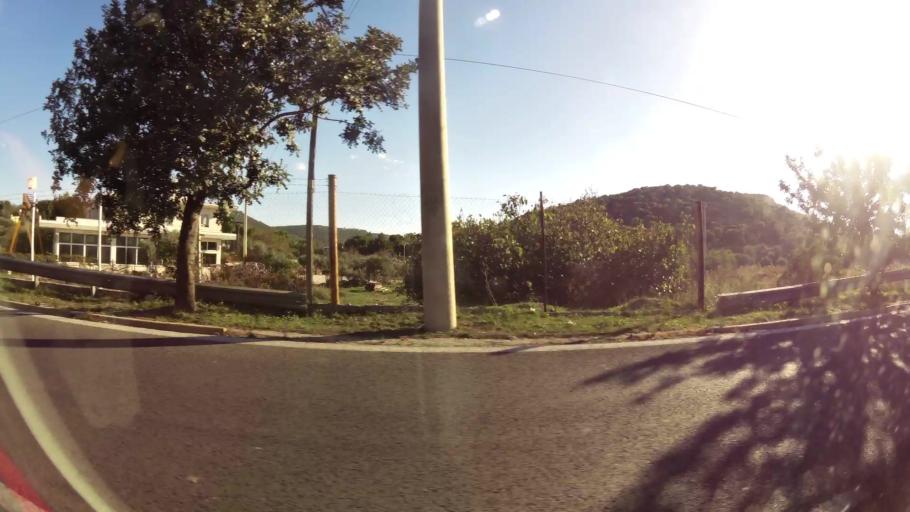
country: GR
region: Attica
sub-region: Nomarchia Anatolikis Attikis
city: Pikermi
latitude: 38.0078
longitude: 23.9639
